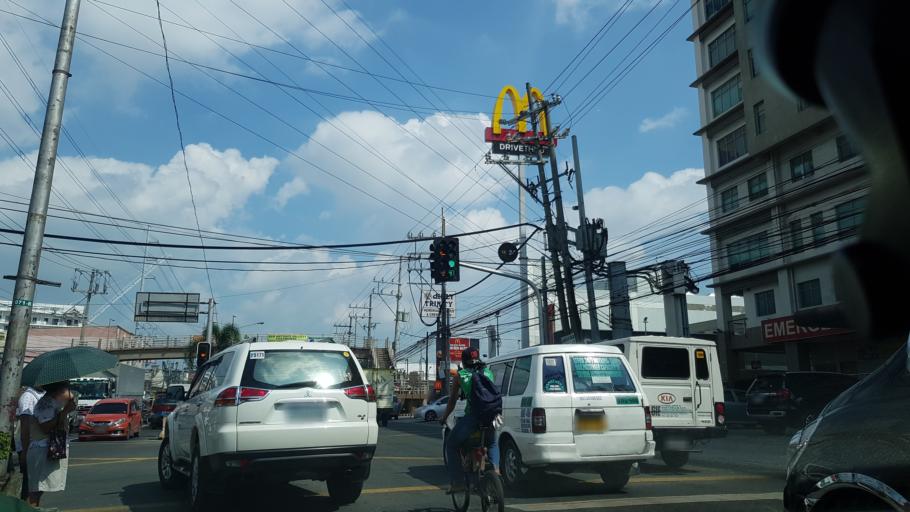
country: PH
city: Sambayanihan People's Village
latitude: 14.4648
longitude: 121.0196
